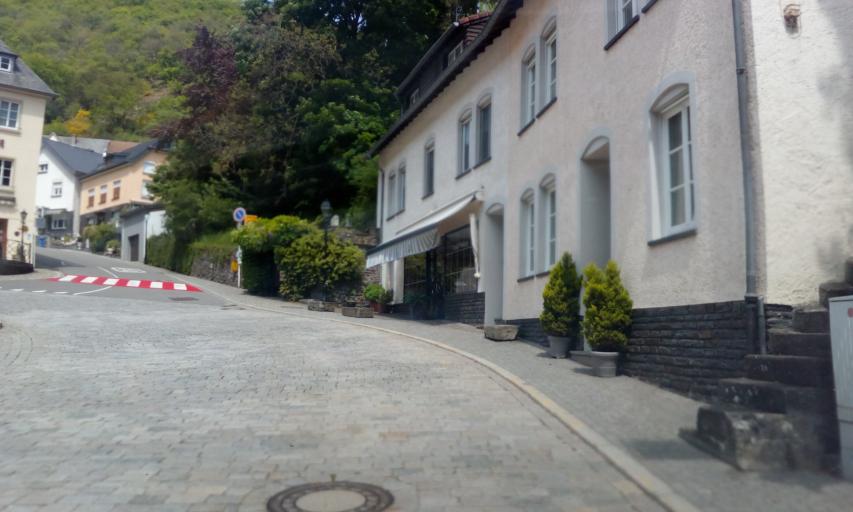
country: LU
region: Diekirch
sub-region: Canton de Vianden
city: Vianden
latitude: 49.9349
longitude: 6.2017
